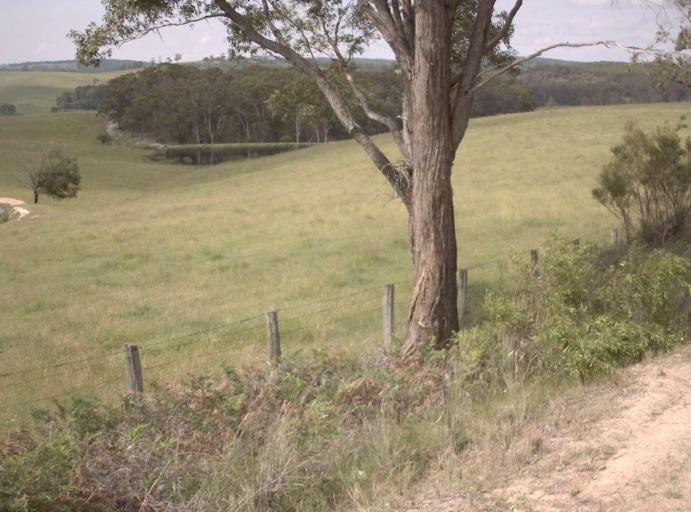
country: AU
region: Victoria
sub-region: Latrobe
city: Traralgon
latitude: -38.3812
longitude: 146.7672
